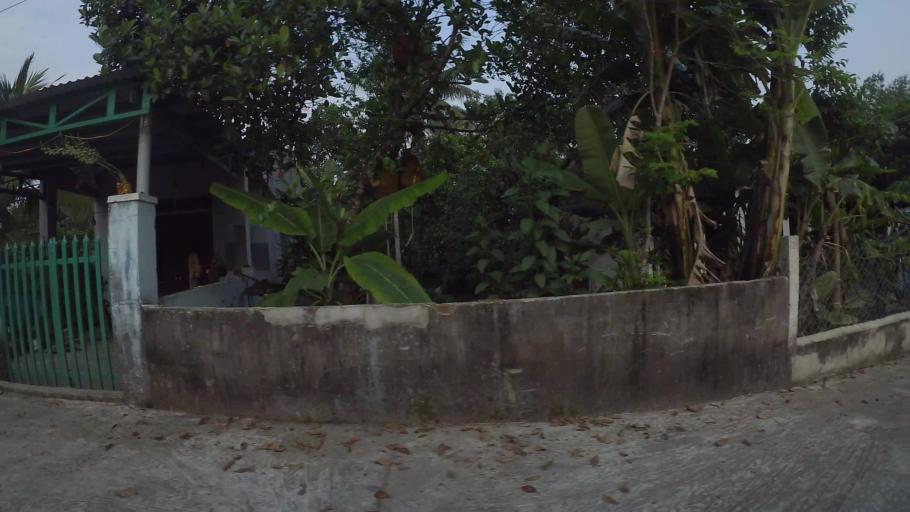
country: VN
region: Da Nang
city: Lien Chieu
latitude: 16.0552
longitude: 108.1071
